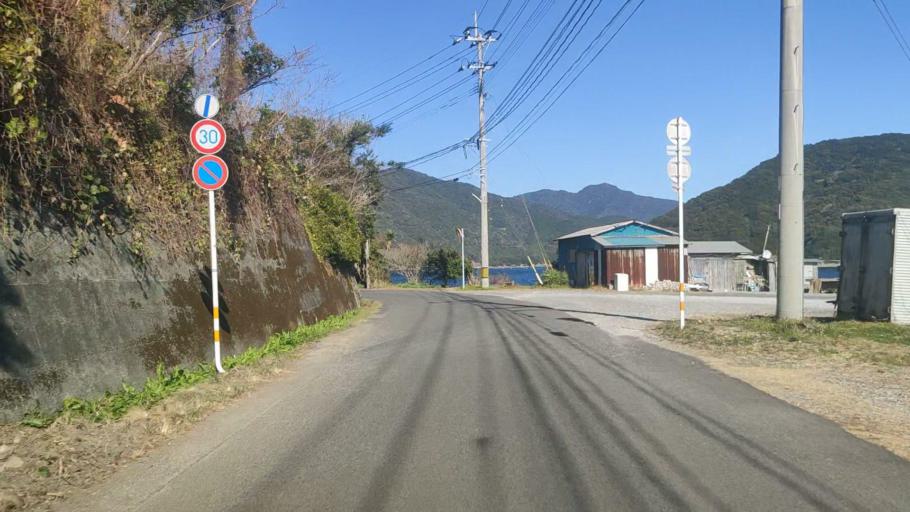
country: JP
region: Oita
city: Saiki
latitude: 32.8310
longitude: 131.9598
